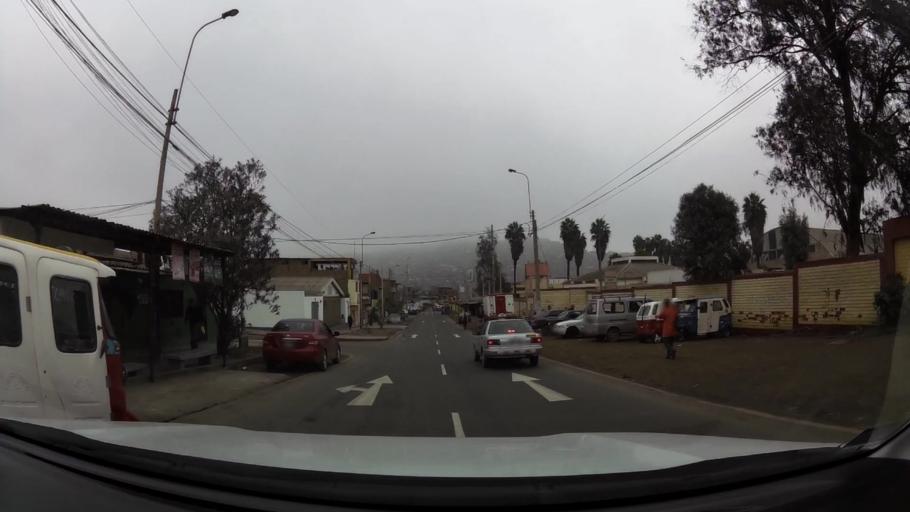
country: PE
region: Lima
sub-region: Lima
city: Surco
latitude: -12.1742
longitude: -76.9455
